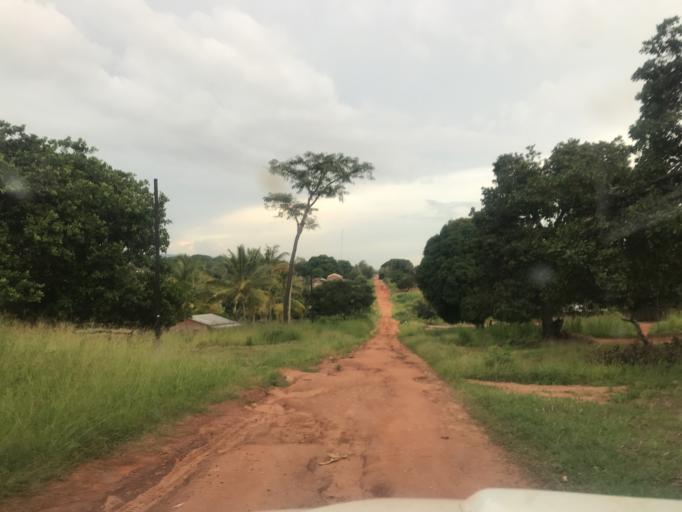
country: TZ
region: Mtwara
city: Newala Kisimani
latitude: -11.3027
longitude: 39.3048
